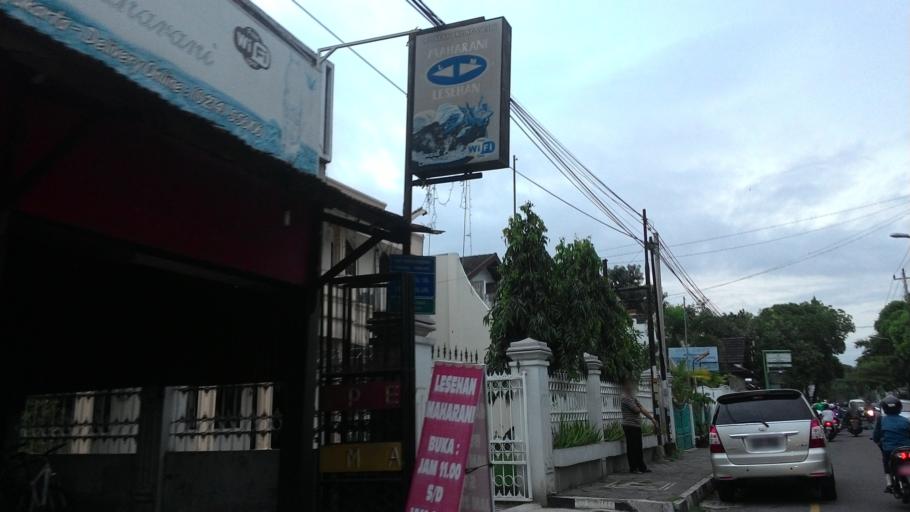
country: ID
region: Daerah Istimewa Yogyakarta
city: Yogyakarta
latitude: -7.7922
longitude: 110.3899
